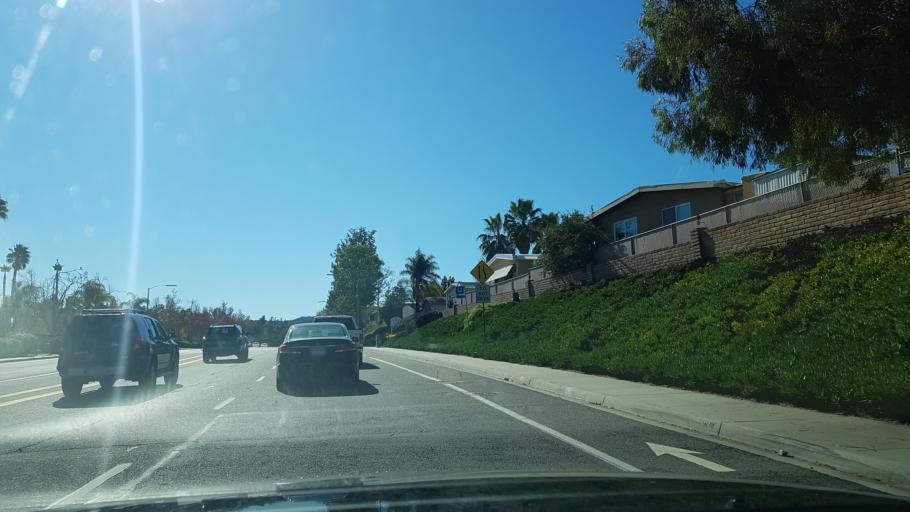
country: US
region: California
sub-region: San Diego County
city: Escondido
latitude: 33.0978
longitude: -117.1109
